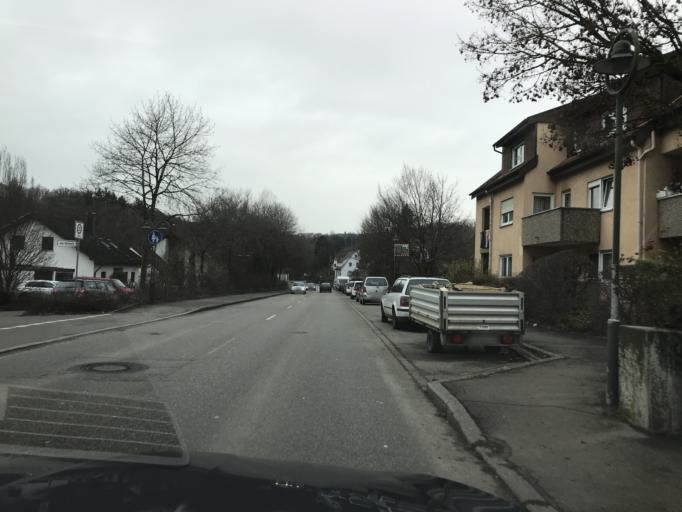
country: DE
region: Baden-Wuerttemberg
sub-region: Regierungsbezirk Stuttgart
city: Nurtingen
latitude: 48.6391
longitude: 9.3158
